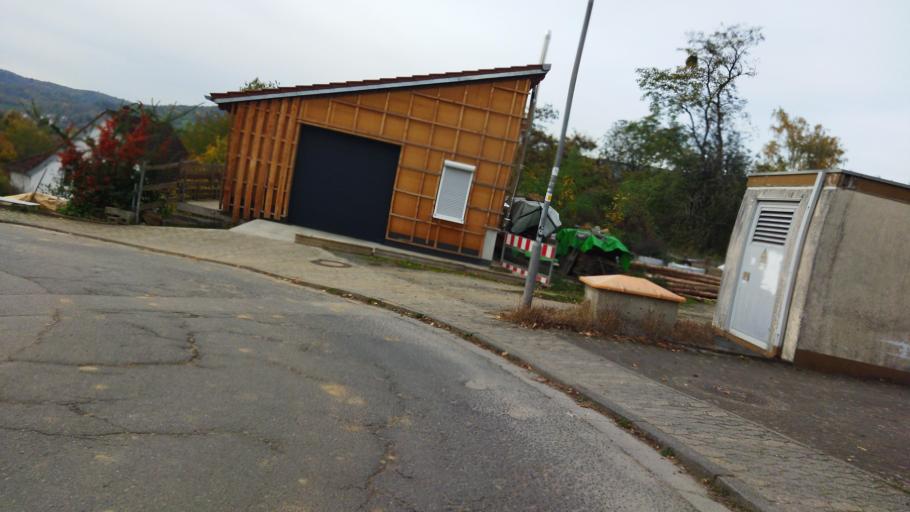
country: DE
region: Hesse
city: Lutzelbach
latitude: 49.7105
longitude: 8.7044
